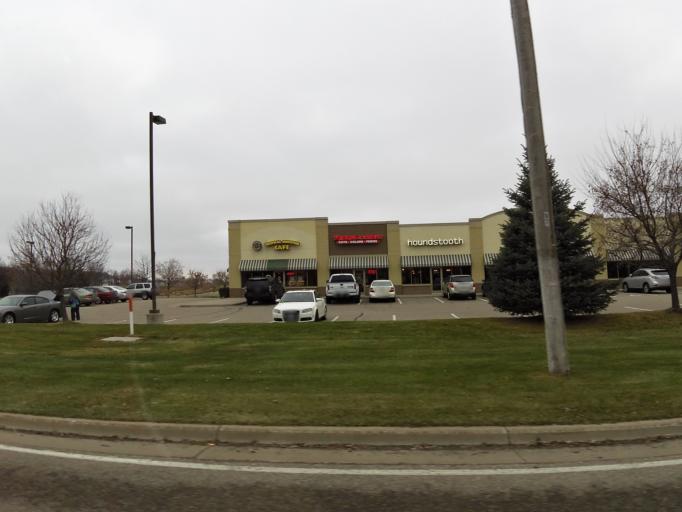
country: US
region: Minnesota
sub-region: Scott County
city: Prior Lake
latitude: 44.7465
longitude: -93.3840
